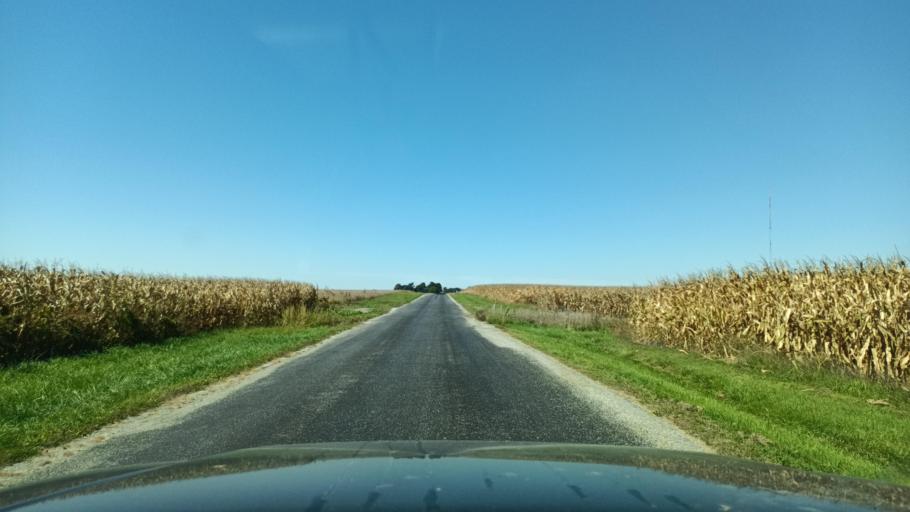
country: US
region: Illinois
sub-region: Champaign County
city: Mahomet
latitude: 40.0986
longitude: -88.4302
